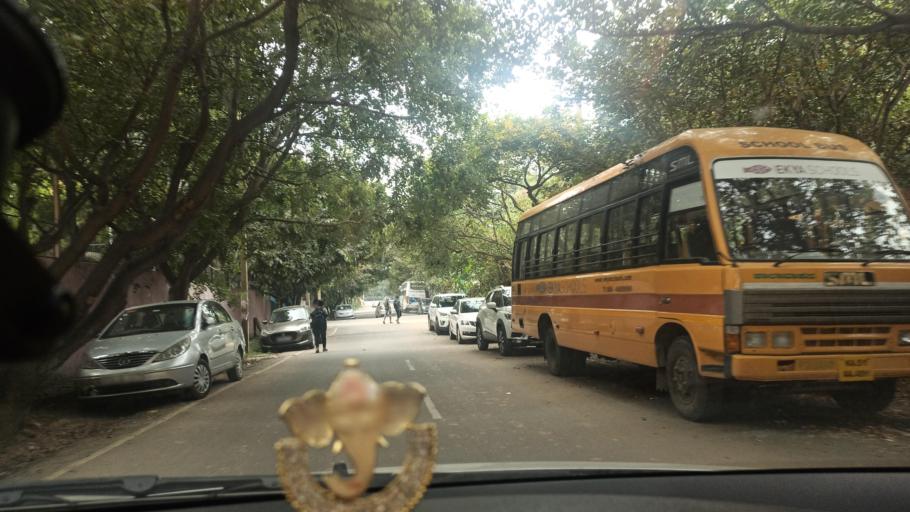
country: IN
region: Karnataka
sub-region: Bangalore Urban
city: Bangalore
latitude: 12.9172
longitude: 77.6432
